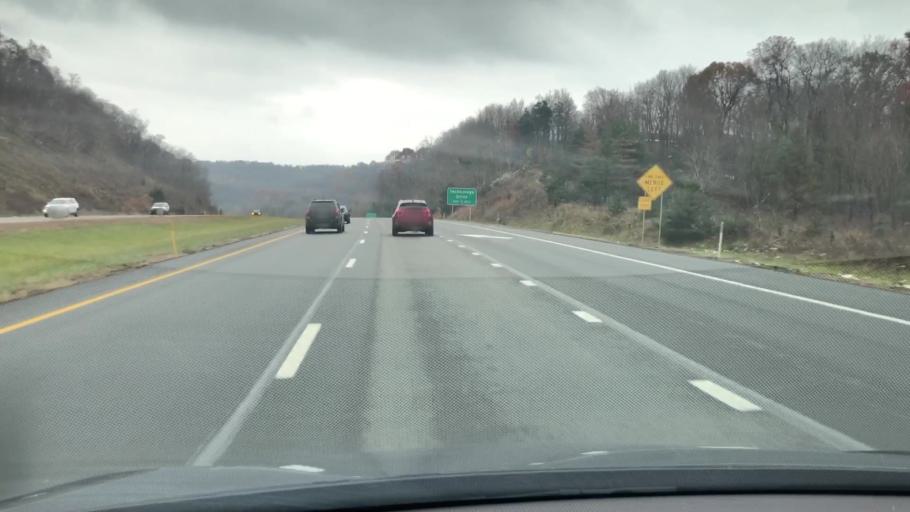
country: US
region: Pennsylvania
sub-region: Westmoreland County
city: New Stanton
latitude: 40.2176
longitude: -79.5920
